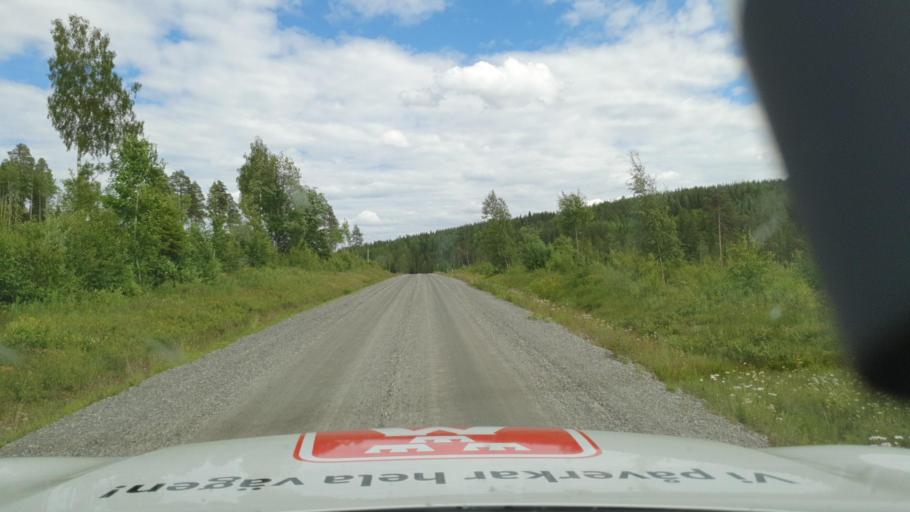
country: SE
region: Vaesterbotten
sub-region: Norsjo Kommun
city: Norsjoe
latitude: 64.8089
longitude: 19.5932
